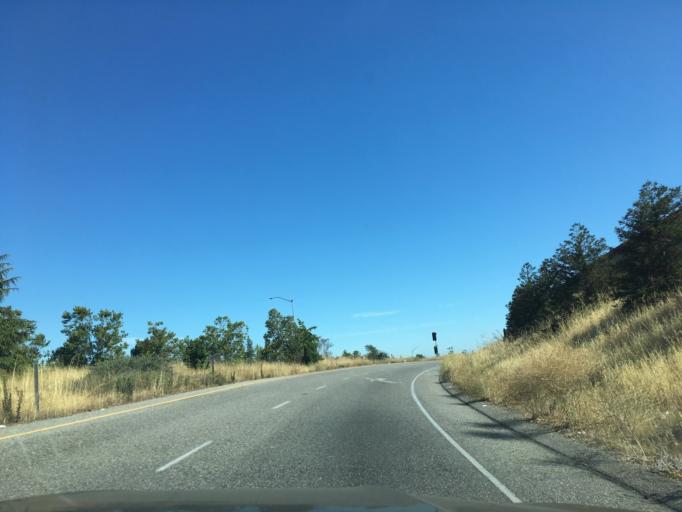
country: US
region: California
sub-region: Santa Clara County
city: Cambrian Park
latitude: 37.2567
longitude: -121.9539
